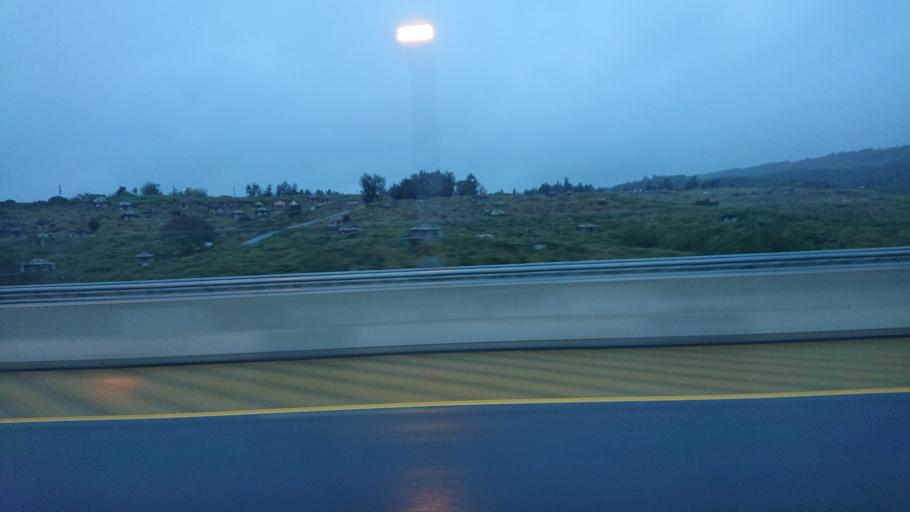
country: TW
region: Taiwan
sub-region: Miaoli
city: Miaoli
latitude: 24.5670
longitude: 120.7143
